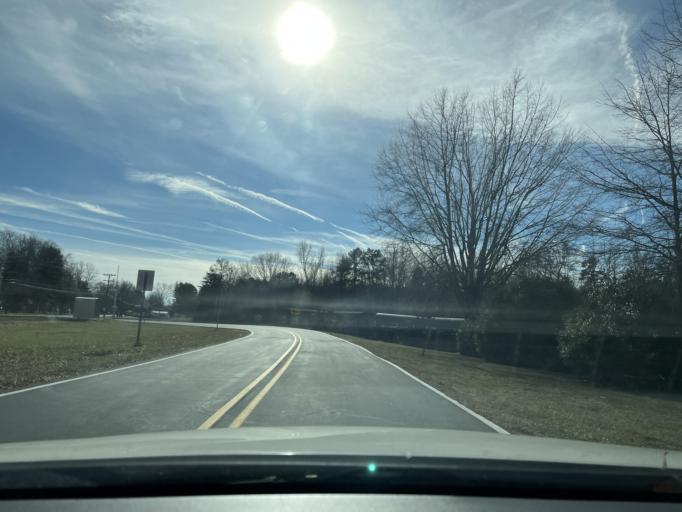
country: US
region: North Carolina
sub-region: Guilford County
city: Pleasant Garden
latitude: 36.0065
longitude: -79.7786
